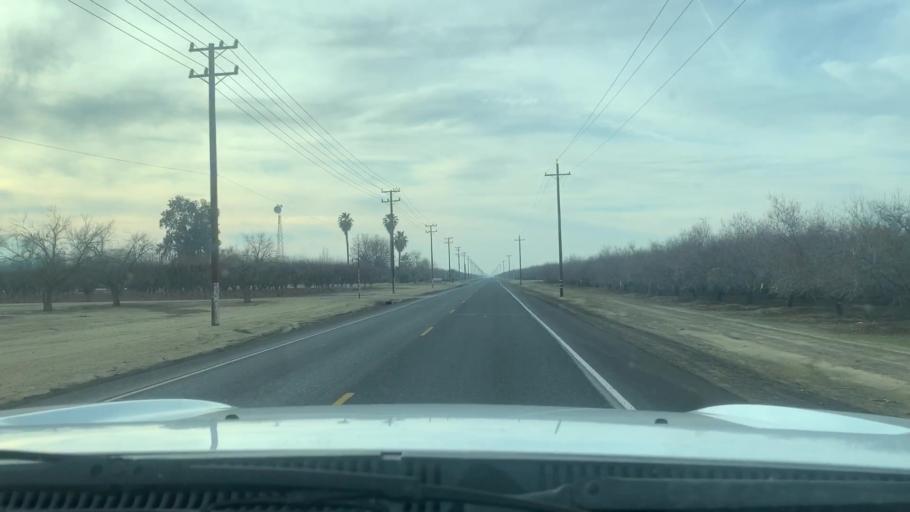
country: US
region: California
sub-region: Kern County
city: Lost Hills
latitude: 35.4993
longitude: -119.6688
